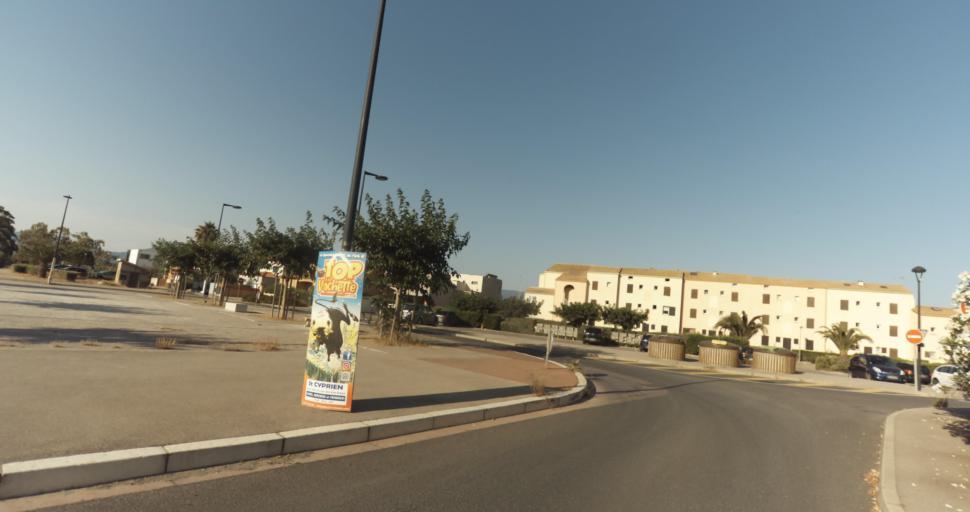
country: FR
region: Languedoc-Roussillon
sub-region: Departement des Pyrenees-Orientales
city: Saint-Cyprien-Plage
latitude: 42.6040
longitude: 3.0396
